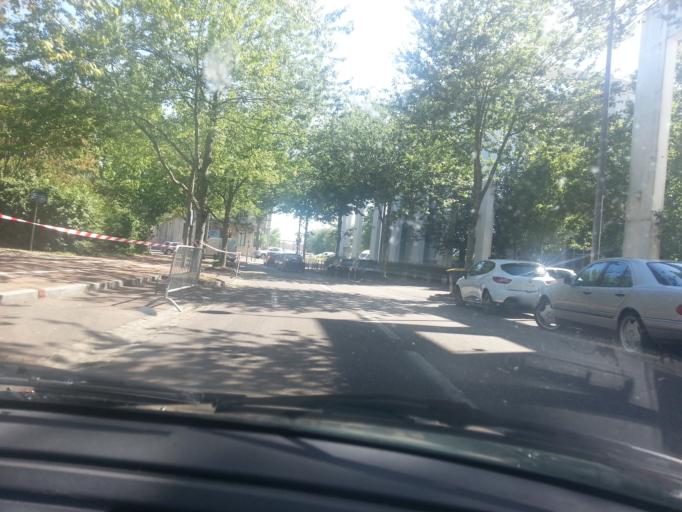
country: FR
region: Bourgogne
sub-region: Departement de Saone-et-Loire
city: Chalon-sur-Saone
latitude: 46.7784
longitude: 4.8456
